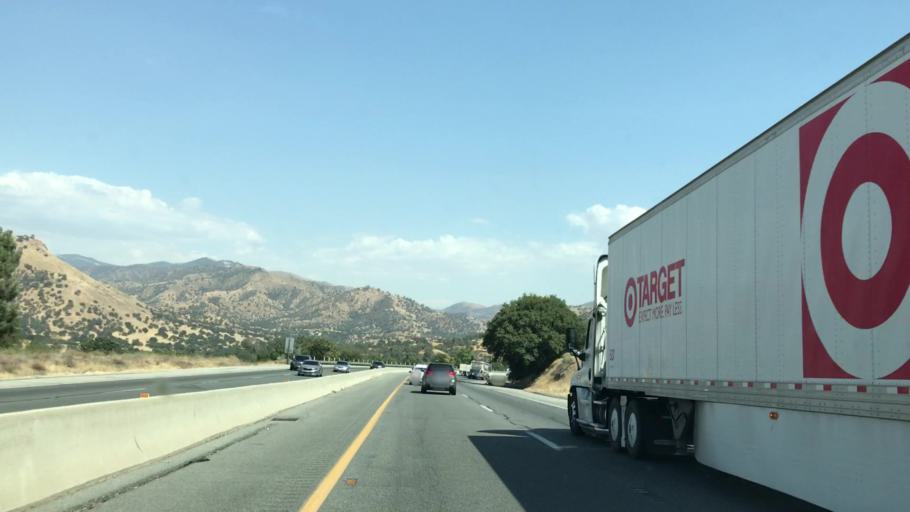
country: US
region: California
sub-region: Kern County
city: Bear Valley Springs
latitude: 35.2449
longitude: -118.5917
